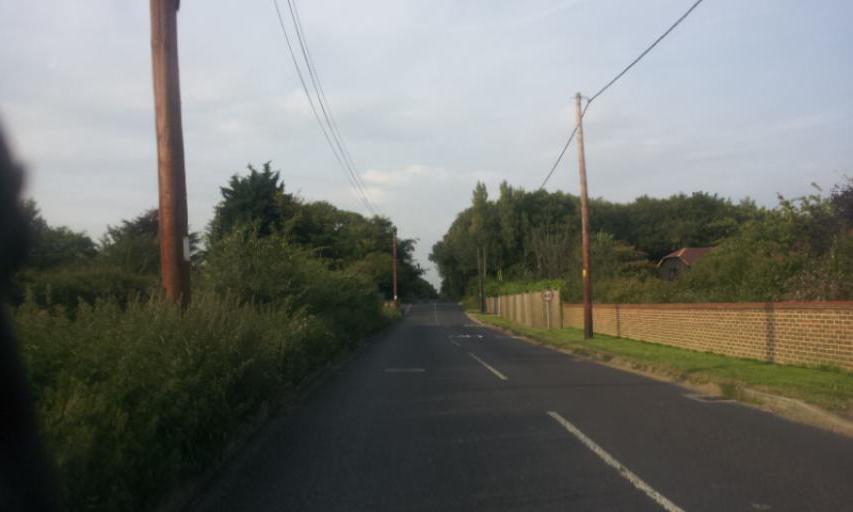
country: GB
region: England
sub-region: Kent
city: Wateringbury
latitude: 51.2688
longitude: 0.4296
